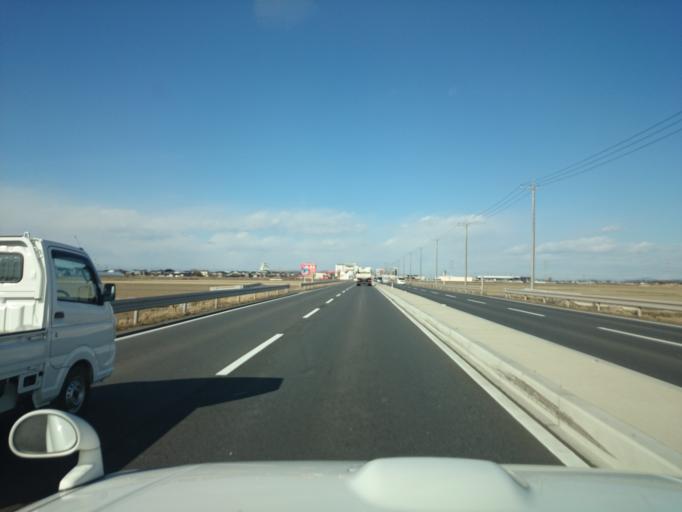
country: JP
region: Ibaraki
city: Ishige
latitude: 36.0989
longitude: 139.9851
